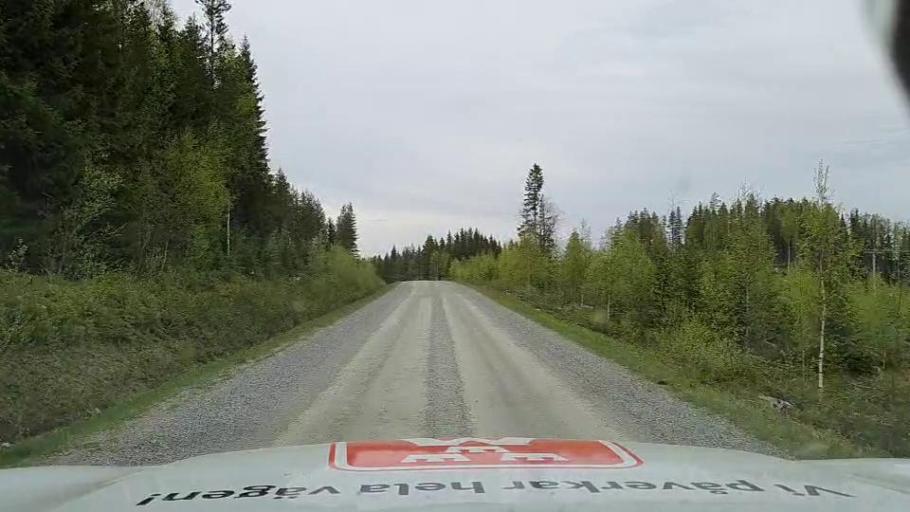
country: SE
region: Jaemtland
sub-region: OEstersunds Kommun
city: Brunflo
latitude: 62.6307
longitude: 14.9407
